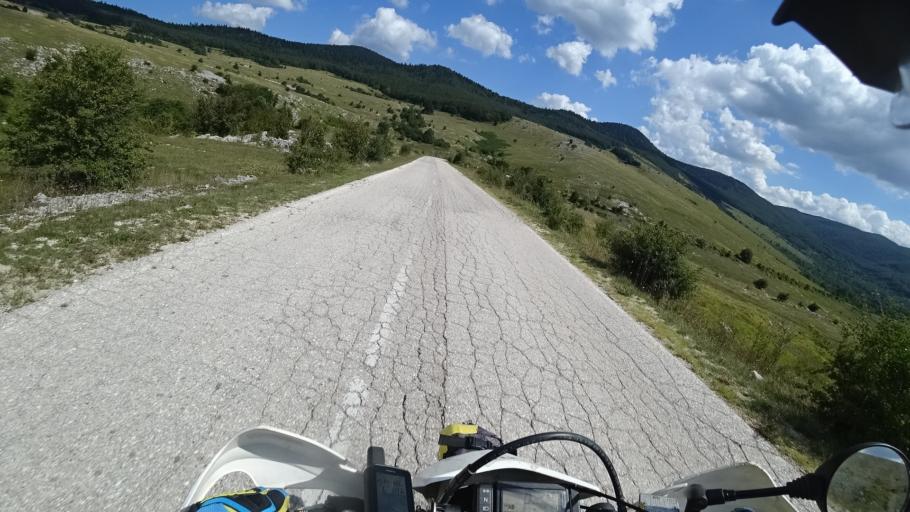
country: BA
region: Federation of Bosnia and Herzegovina
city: Orasac
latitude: 44.4736
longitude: 15.9774
